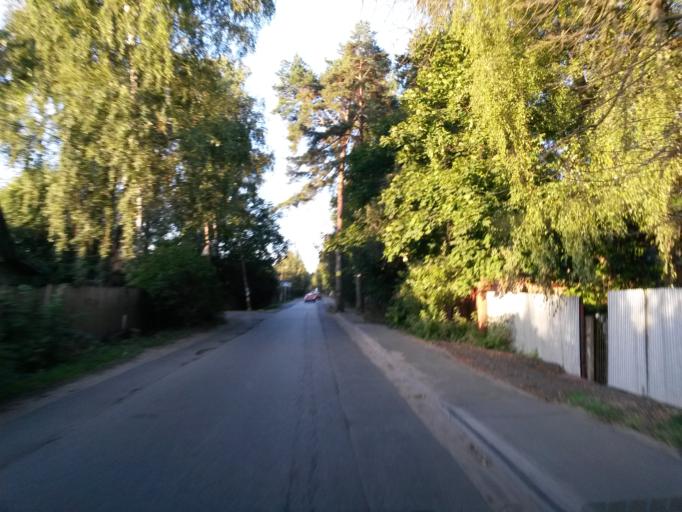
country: RU
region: Moskovskaya
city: Mamontovka
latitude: 55.9852
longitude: 37.8457
